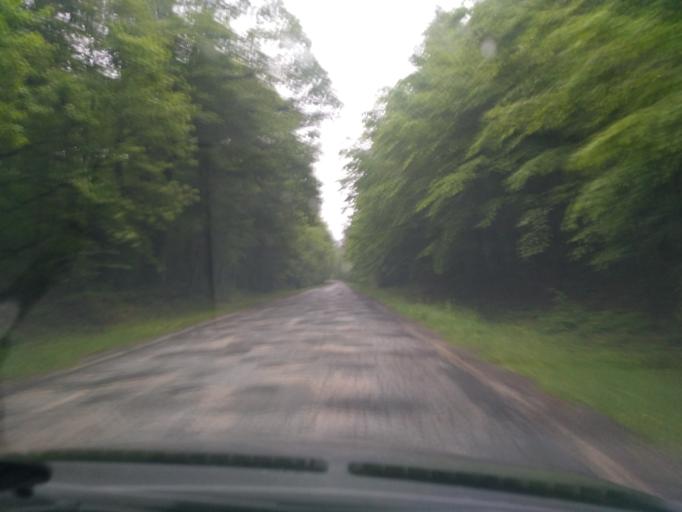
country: PL
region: Subcarpathian Voivodeship
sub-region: Powiat debicki
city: Pilzno
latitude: 49.9743
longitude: 21.3725
